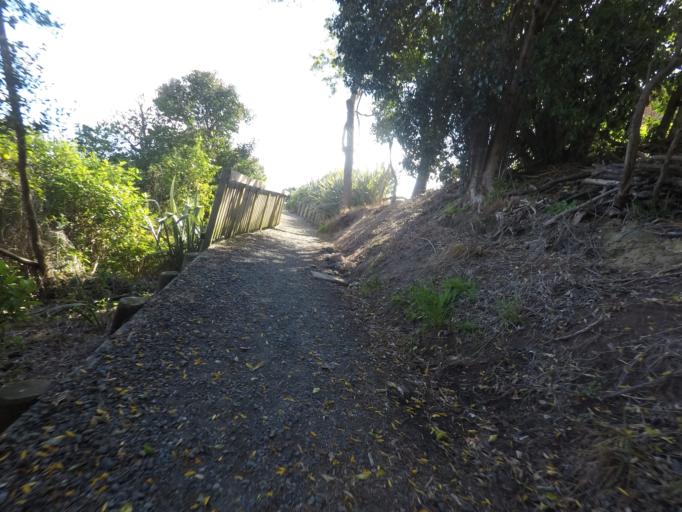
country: NZ
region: Auckland
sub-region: Auckland
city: Rosebank
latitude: -36.8561
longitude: 174.7124
